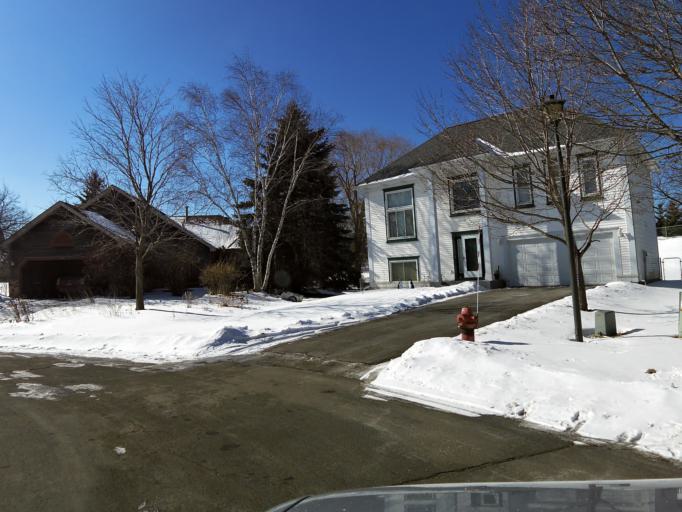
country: US
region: Minnesota
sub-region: Washington County
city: Woodbury
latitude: 44.9362
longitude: -92.9328
